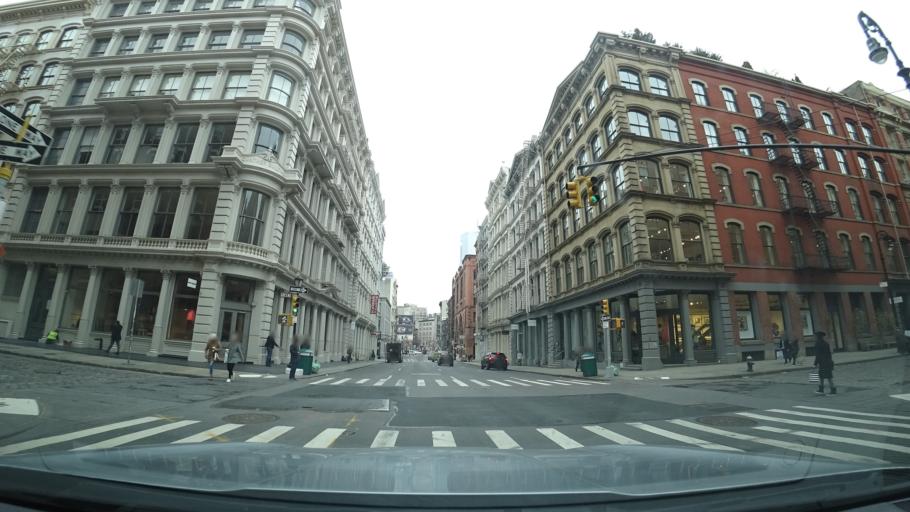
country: US
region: New York
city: New York City
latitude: 40.7225
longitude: -74.0013
